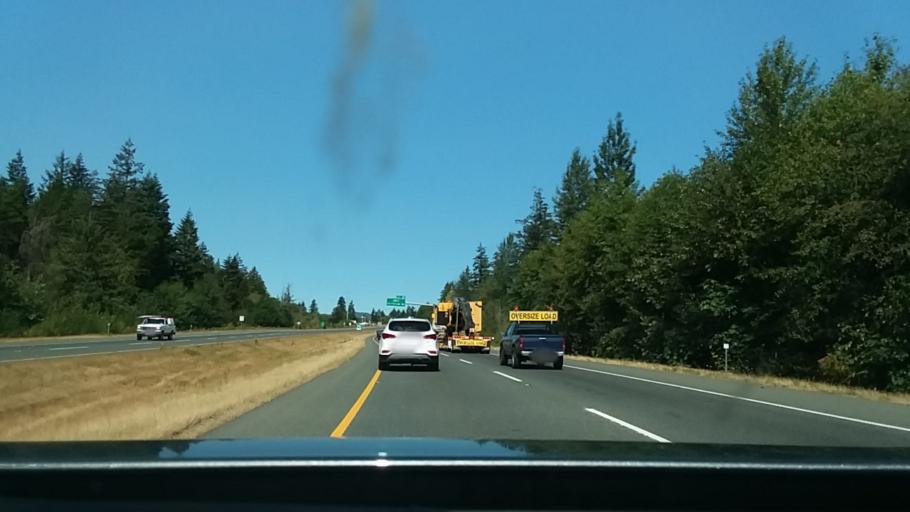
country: CA
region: British Columbia
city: Nanaimo
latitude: 49.1859
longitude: -123.9930
